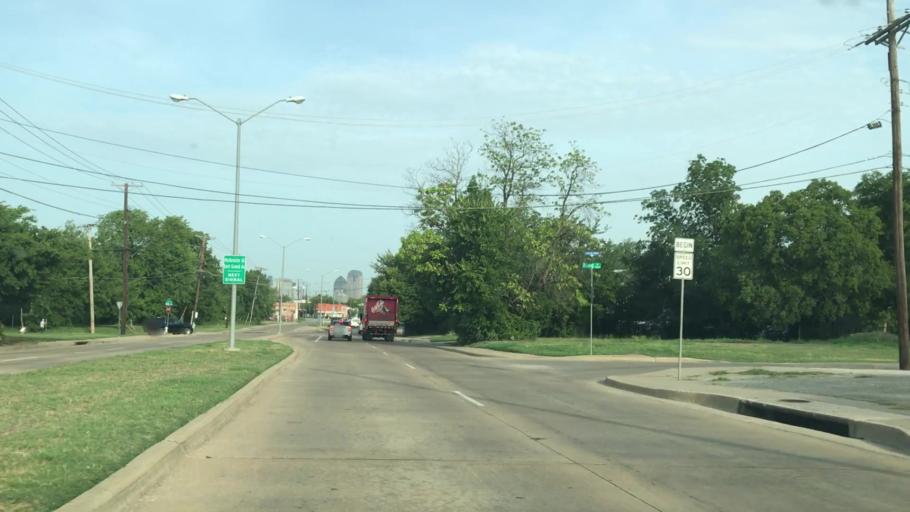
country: US
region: Texas
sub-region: Dallas County
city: Dallas
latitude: 32.7838
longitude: -96.7552
